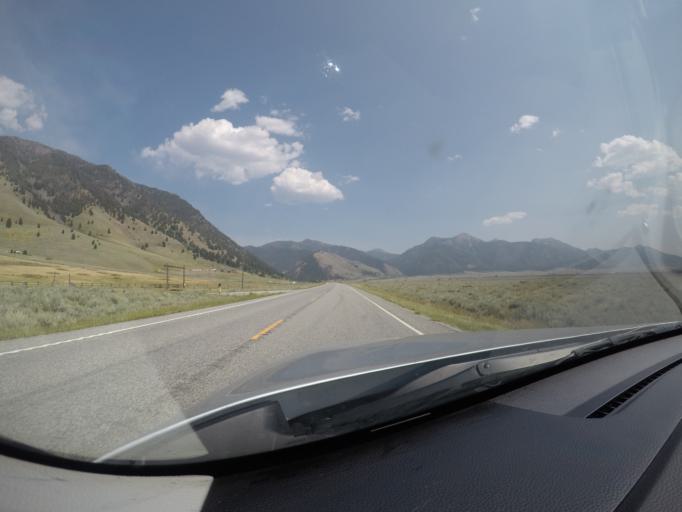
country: US
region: Montana
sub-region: Gallatin County
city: West Yellowstone
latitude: 44.8292
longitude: -111.4737
